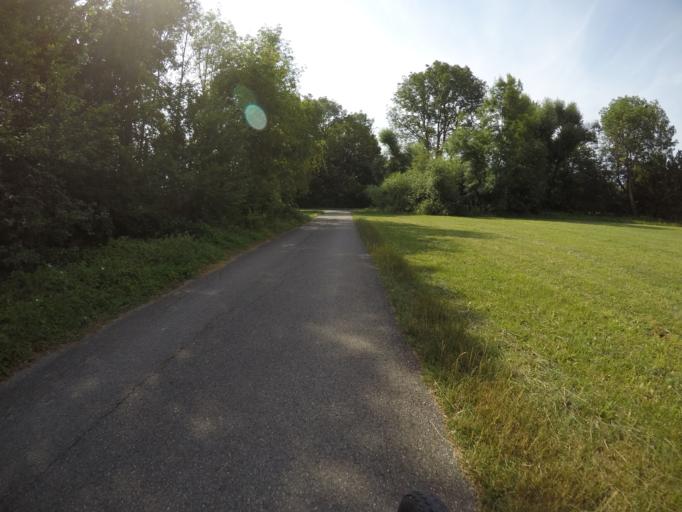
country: DE
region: Baden-Wuerttemberg
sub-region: Regierungsbezirk Stuttgart
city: Steinenbronn
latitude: 48.7198
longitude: 9.1199
